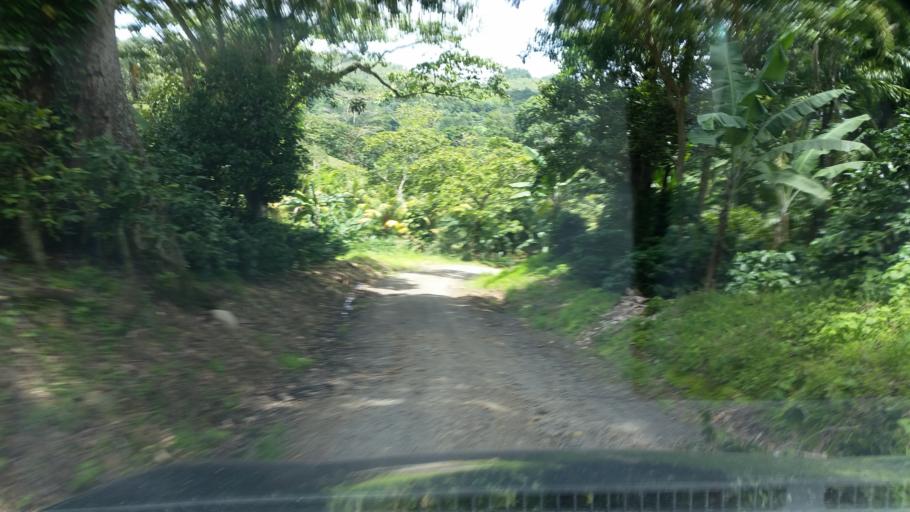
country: NI
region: Atlantico Norte (RAAN)
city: Waslala
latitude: 13.2591
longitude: -85.6205
